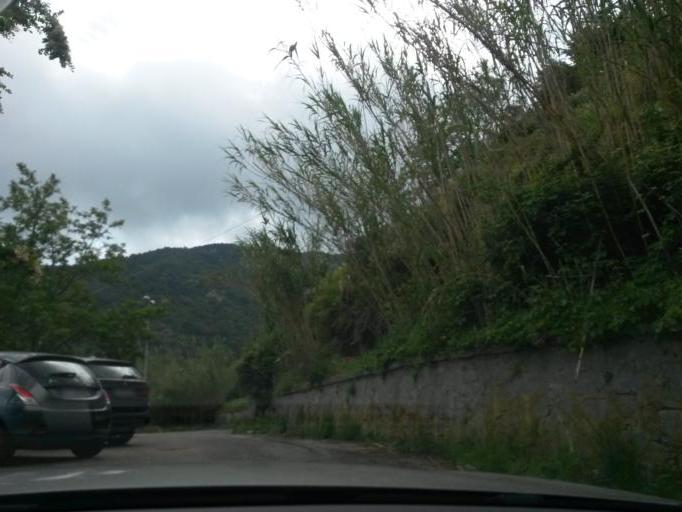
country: IT
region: Tuscany
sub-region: Provincia di Livorno
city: Marciana
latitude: 42.7858
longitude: 10.1855
